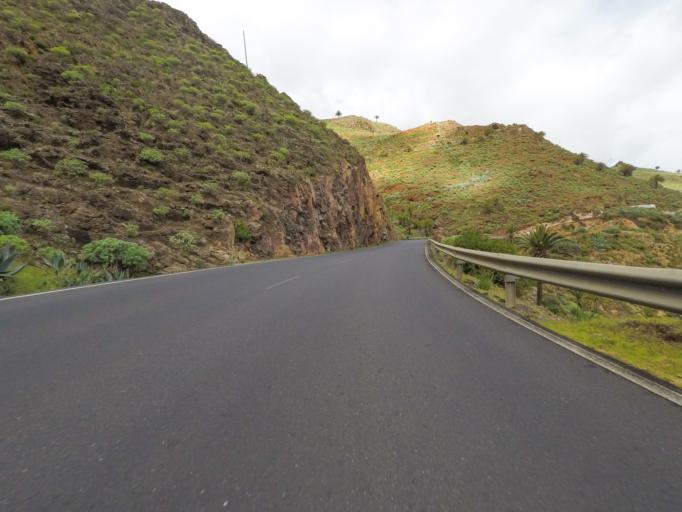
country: ES
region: Canary Islands
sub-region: Provincia de Santa Cruz de Tenerife
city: San Sebastian de la Gomera
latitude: 28.0976
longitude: -17.1734
